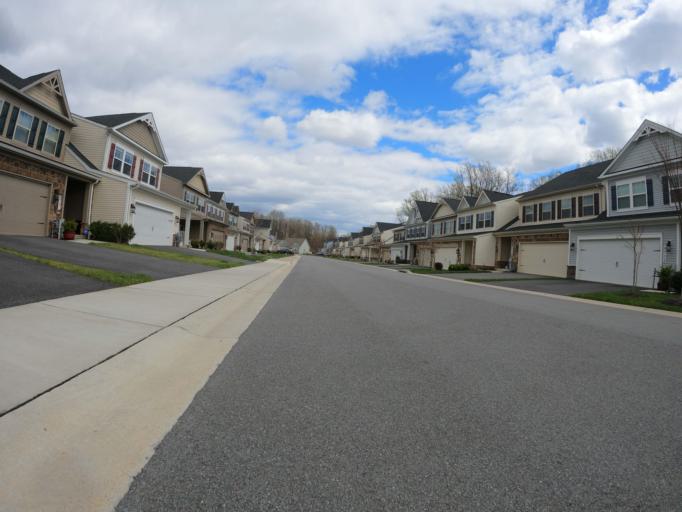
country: US
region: Maryland
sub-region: Howard County
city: North Laurel
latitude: 39.1435
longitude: -76.8540
